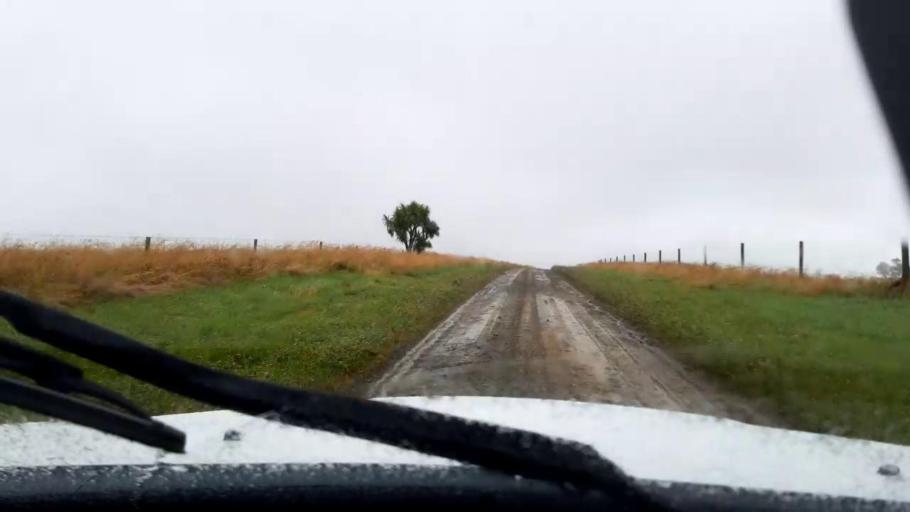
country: NZ
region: Canterbury
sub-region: Timaru District
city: Pleasant Point
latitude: -44.1691
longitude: 171.1626
